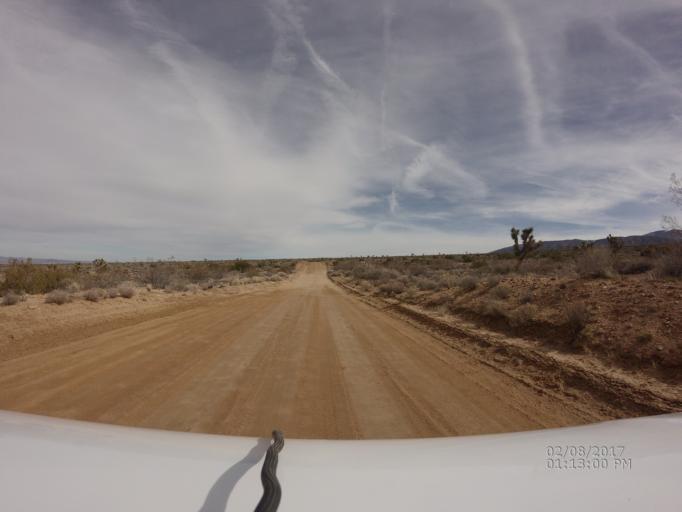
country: US
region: California
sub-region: Los Angeles County
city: Lake Los Angeles
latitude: 34.4749
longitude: -117.7884
